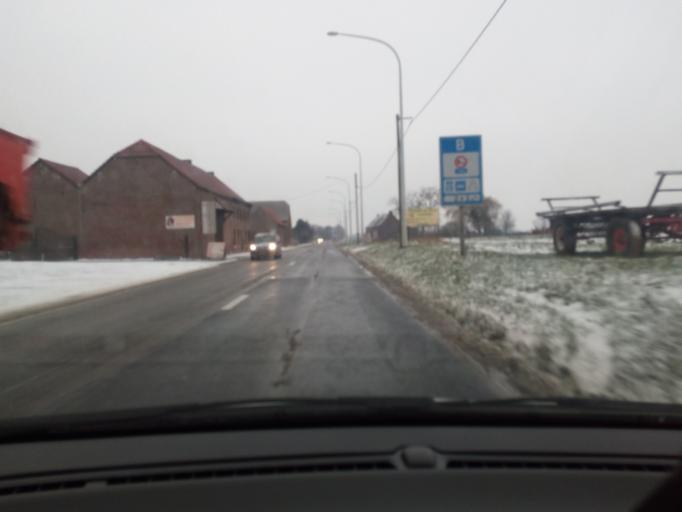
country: FR
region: Nord-Pas-de-Calais
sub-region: Departement du Nord
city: La Longueville
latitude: 50.3400
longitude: 3.8756
